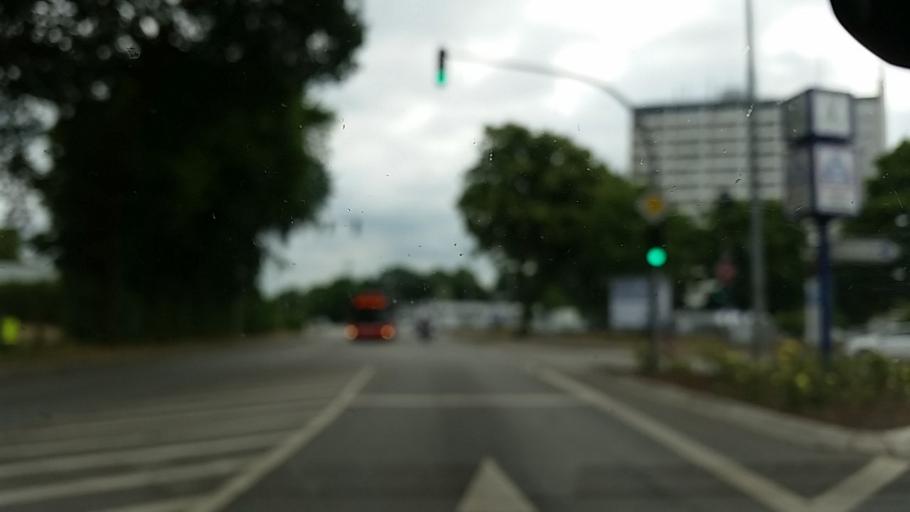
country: DE
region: Hamburg
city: Hummelsbuettel
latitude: 53.6886
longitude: 10.0371
